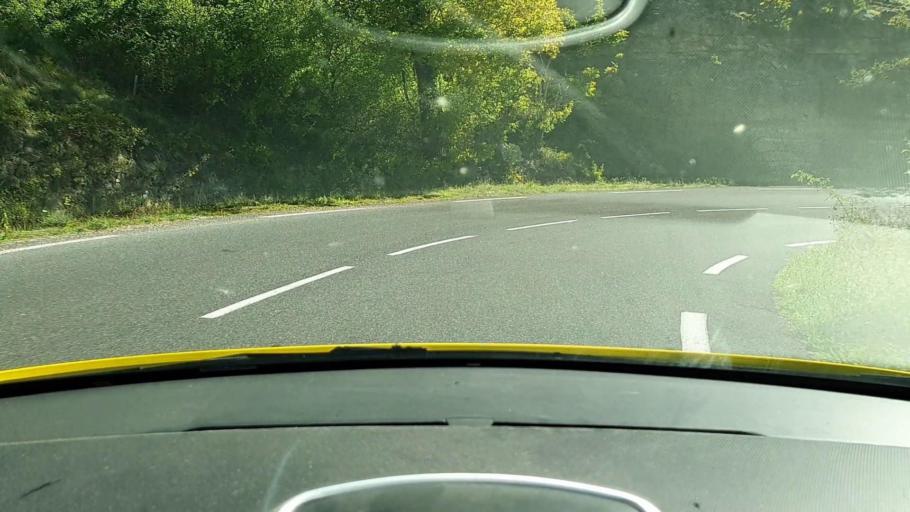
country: FR
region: Languedoc-Roussillon
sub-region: Departement du Gard
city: Le Vigan
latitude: 43.9673
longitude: 3.4433
